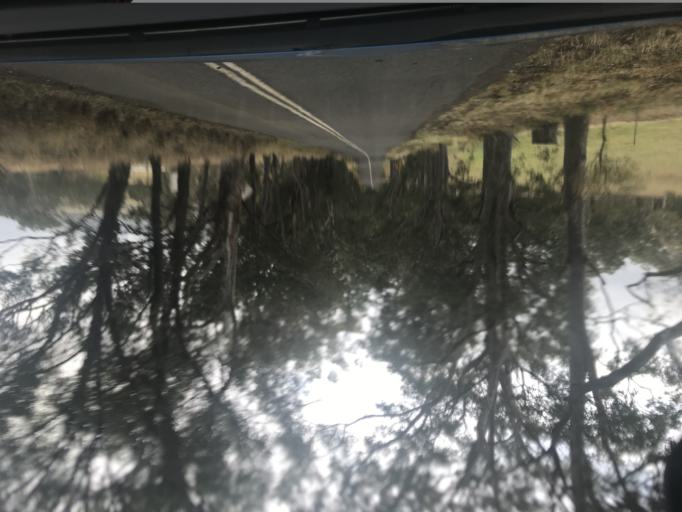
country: AU
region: New South Wales
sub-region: Cessnock
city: Cessnock
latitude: -32.8107
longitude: 151.3032
